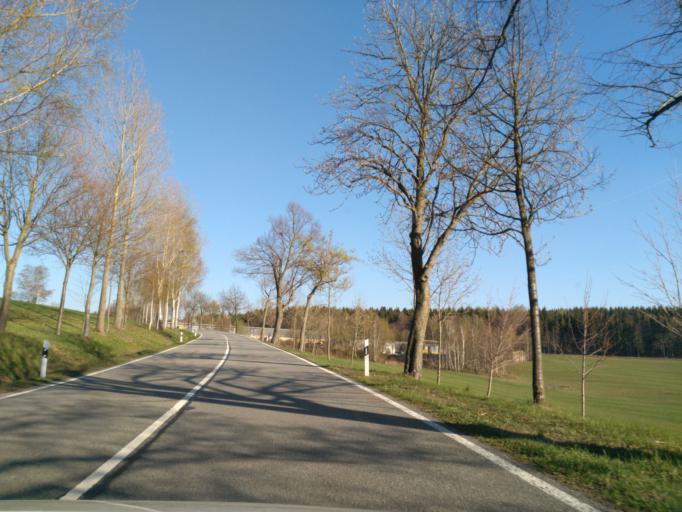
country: DE
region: Saxony
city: Schlettau
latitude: 50.5549
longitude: 12.9750
